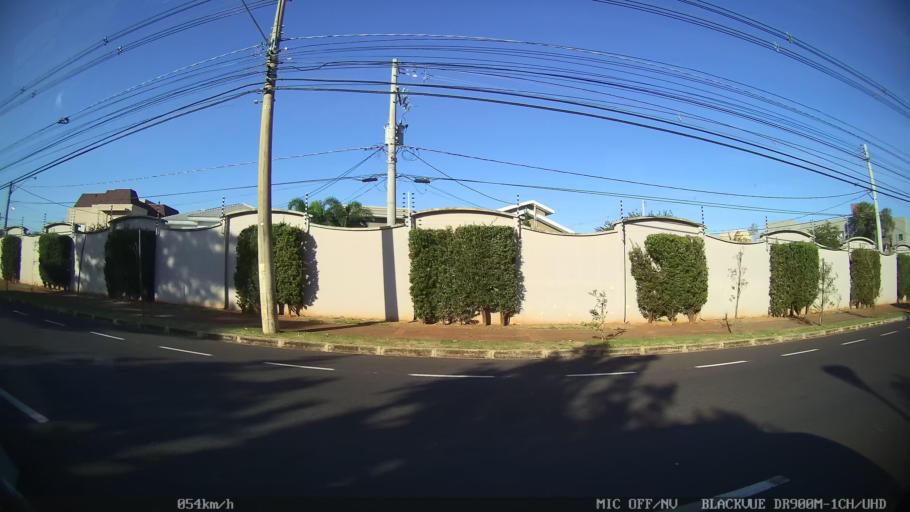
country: BR
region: Sao Paulo
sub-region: Sao Jose Do Rio Preto
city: Sao Jose do Rio Preto
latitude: -20.8591
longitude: -49.4117
